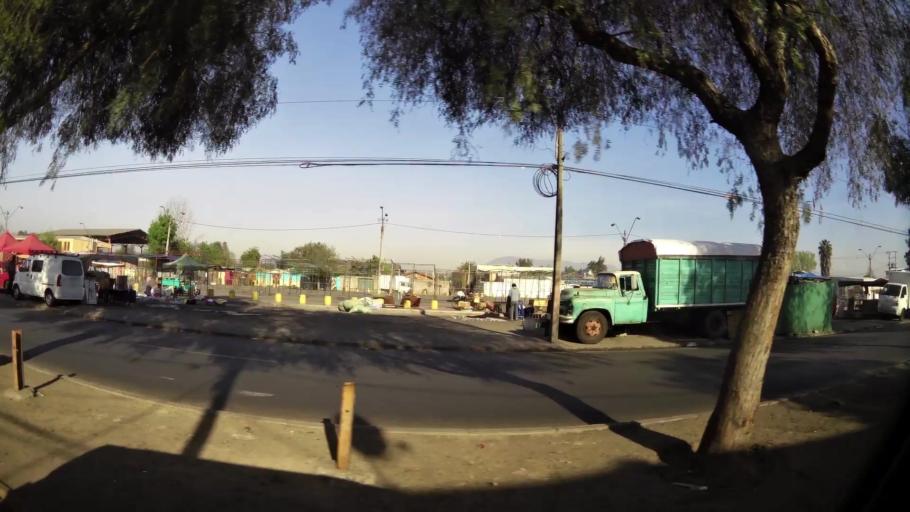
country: CL
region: Santiago Metropolitan
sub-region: Provincia de Santiago
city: Lo Prado
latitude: -33.4398
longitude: -70.7407
